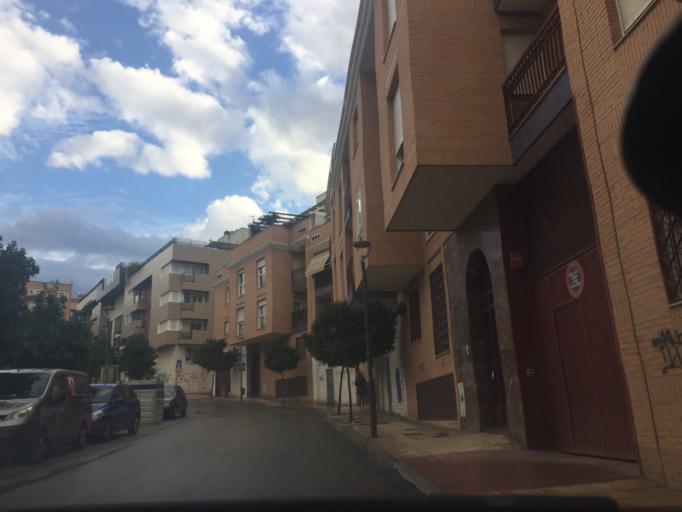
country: ES
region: Andalusia
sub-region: Provincia de Jaen
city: Jaen
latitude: 37.7730
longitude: -3.7837
